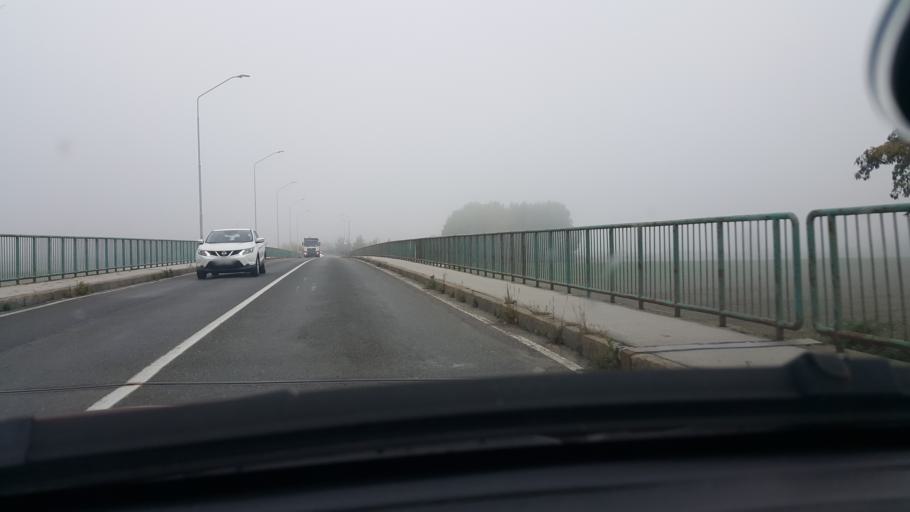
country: SI
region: Brezice
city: Brezice
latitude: 45.8942
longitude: 15.6034
